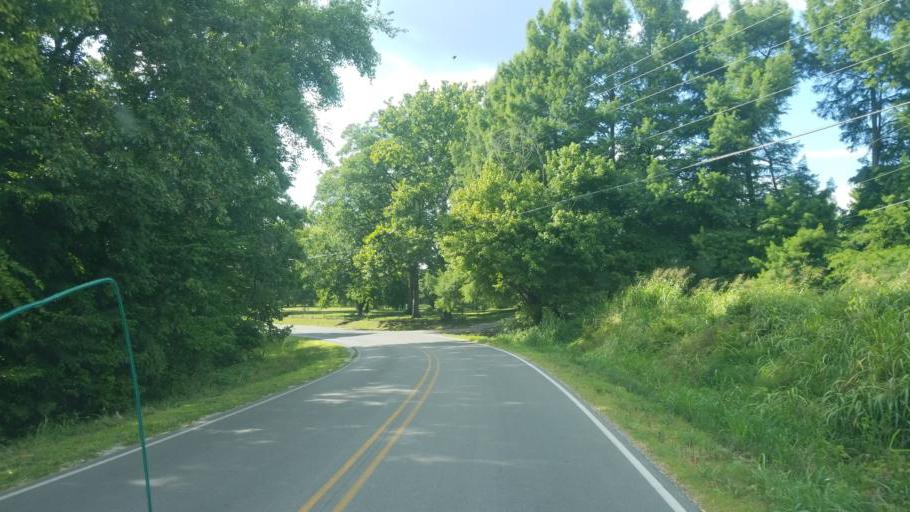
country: US
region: Illinois
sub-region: Union County
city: Cobden
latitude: 37.5613
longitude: -89.3060
